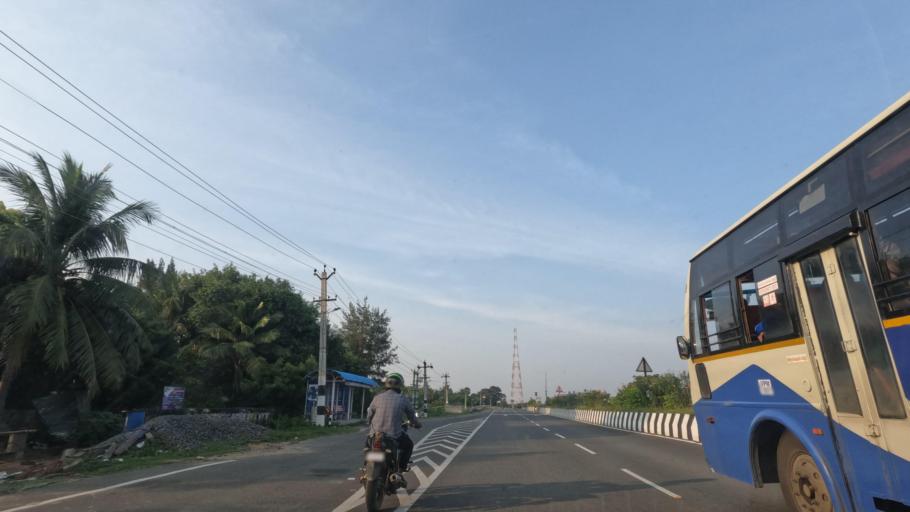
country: IN
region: Tamil Nadu
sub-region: Kancheepuram
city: Mamallapuram
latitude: 12.7058
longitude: 80.2239
